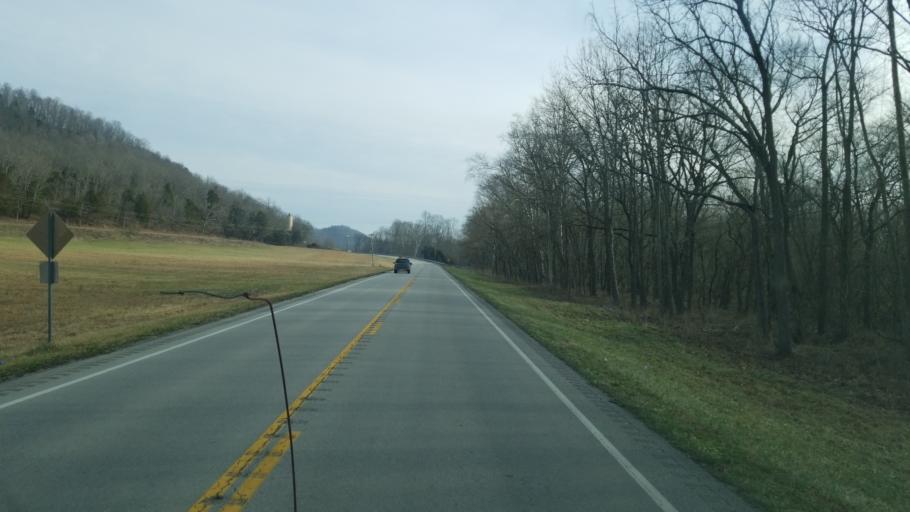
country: US
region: Kentucky
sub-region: Casey County
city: Liberty
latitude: 37.3386
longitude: -84.9044
